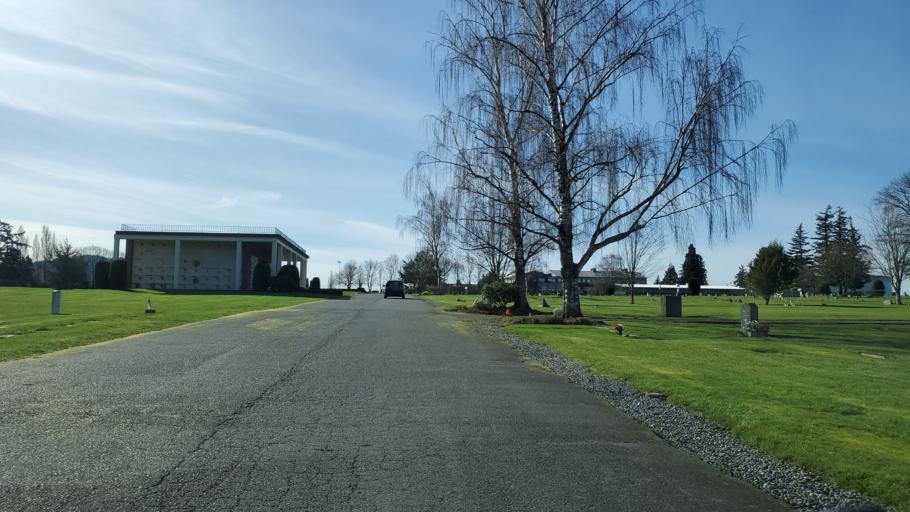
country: US
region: Washington
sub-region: Skagit County
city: Mount Vernon
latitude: 48.4281
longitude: -122.3262
